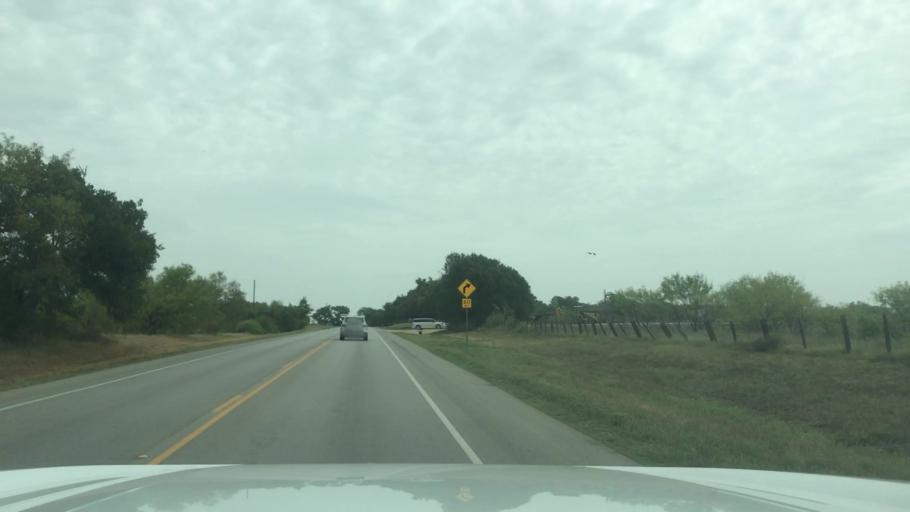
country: US
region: Texas
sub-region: Erath County
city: Dublin
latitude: 32.0975
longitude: -98.4020
